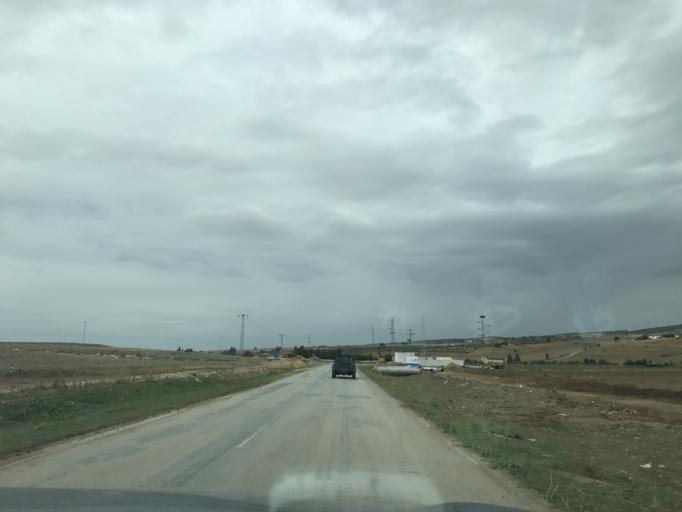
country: TN
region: Silyanah
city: Bu `Aradah
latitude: 36.2061
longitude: 9.7246
